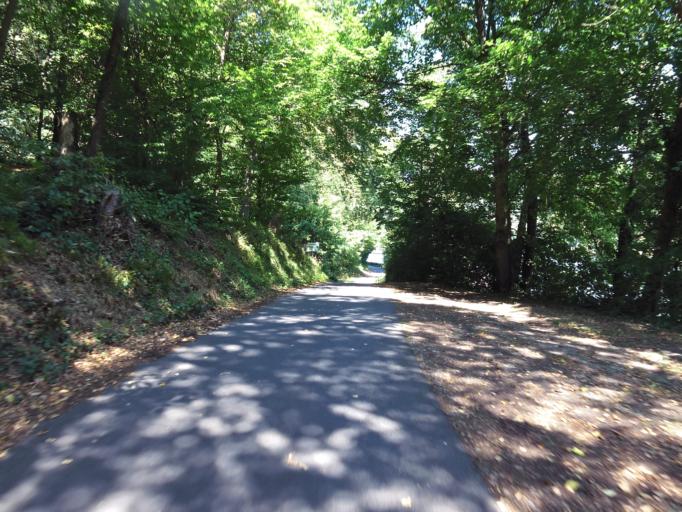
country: DE
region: Baden-Wuerttemberg
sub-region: Karlsruhe Region
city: Zwingenberg
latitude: 49.4270
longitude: 9.0017
